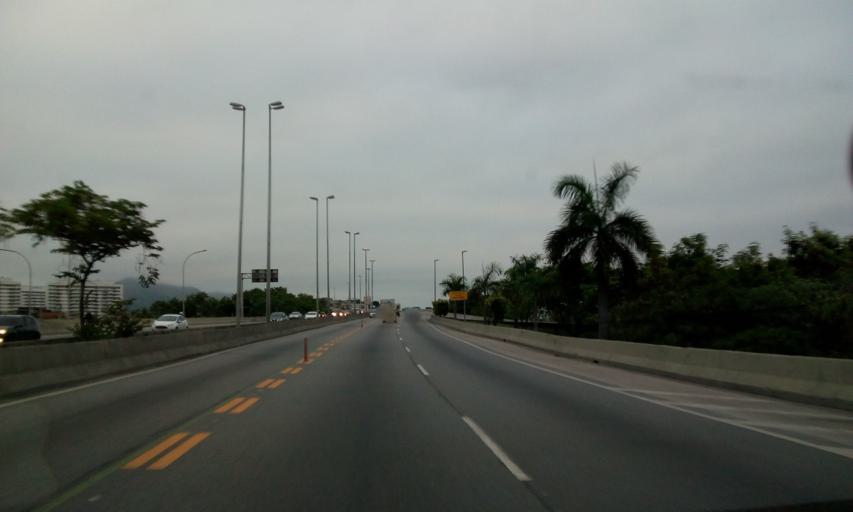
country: BR
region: Rio de Janeiro
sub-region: Rio De Janeiro
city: Rio de Janeiro
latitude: -22.8822
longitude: -43.2853
